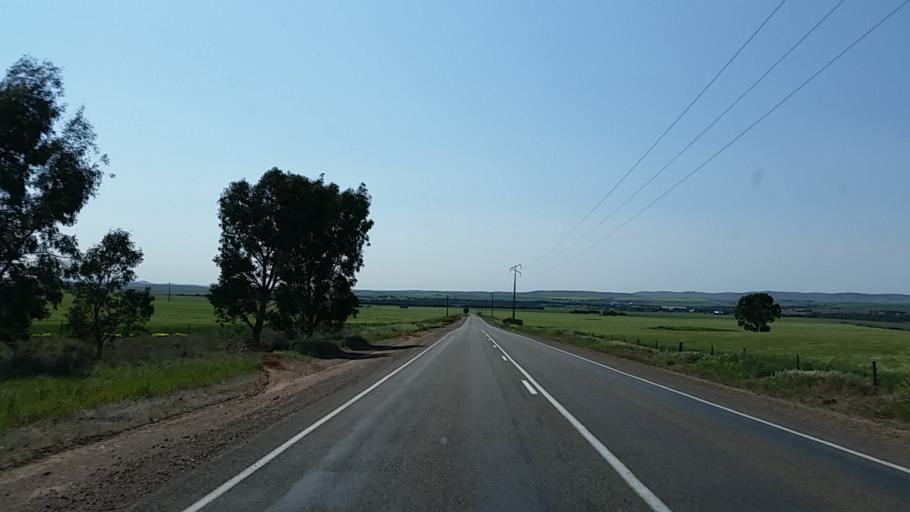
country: AU
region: South Australia
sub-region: Port Pirie City and Dists
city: Crystal Brook
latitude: -33.2774
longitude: 138.2983
